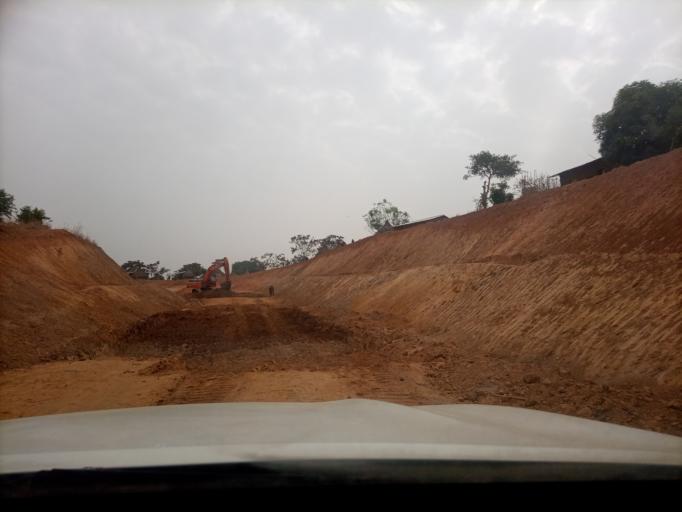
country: ET
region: Oromiya
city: Mendi
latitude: 10.2004
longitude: 35.0691
